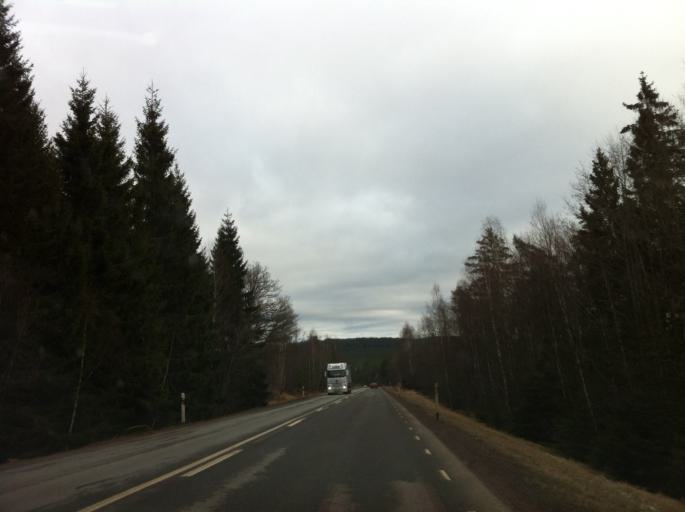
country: SE
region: Kalmar
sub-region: Vimmerby Kommun
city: Vimmerby
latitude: 57.6339
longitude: 15.7265
